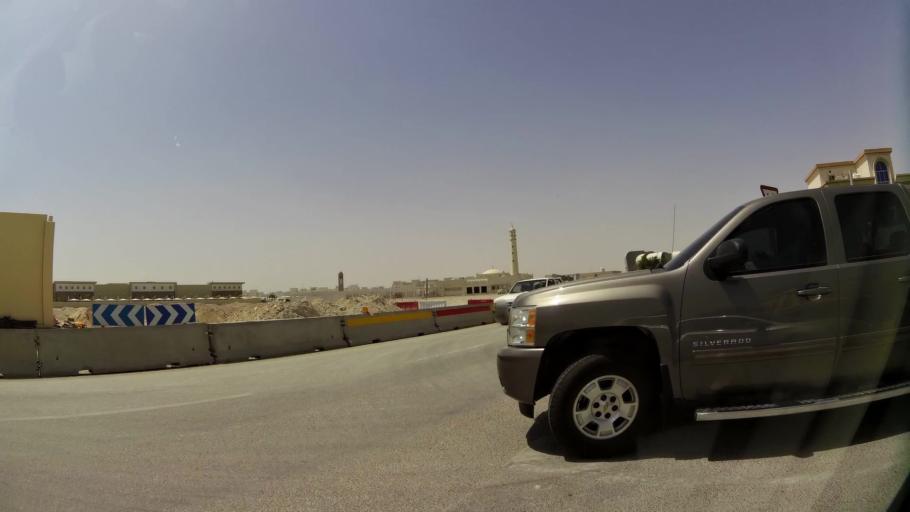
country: QA
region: Baladiyat Umm Salal
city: Umm Salal Muhammad
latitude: 25.3715
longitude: 51.4750
